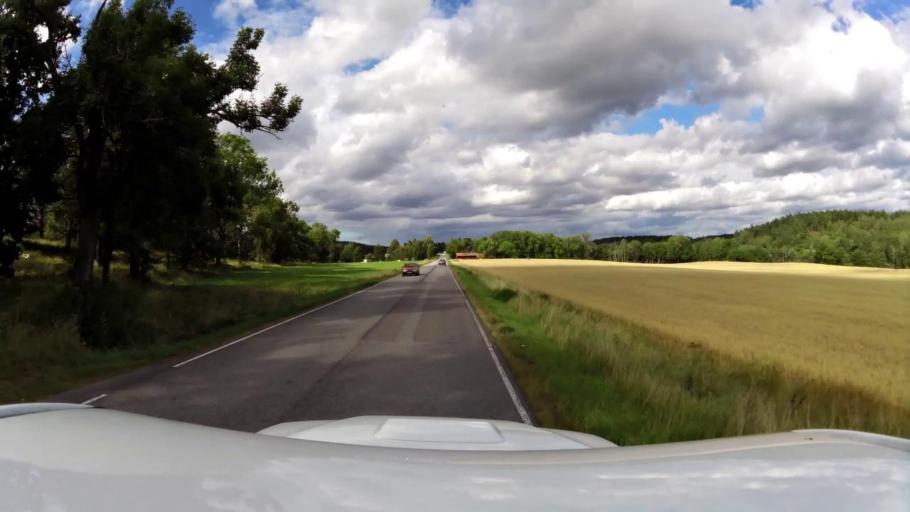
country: SE
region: OEstergoetland
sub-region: Linkopings Kommun
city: Sturefors
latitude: 58.3071
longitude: 15.7259
